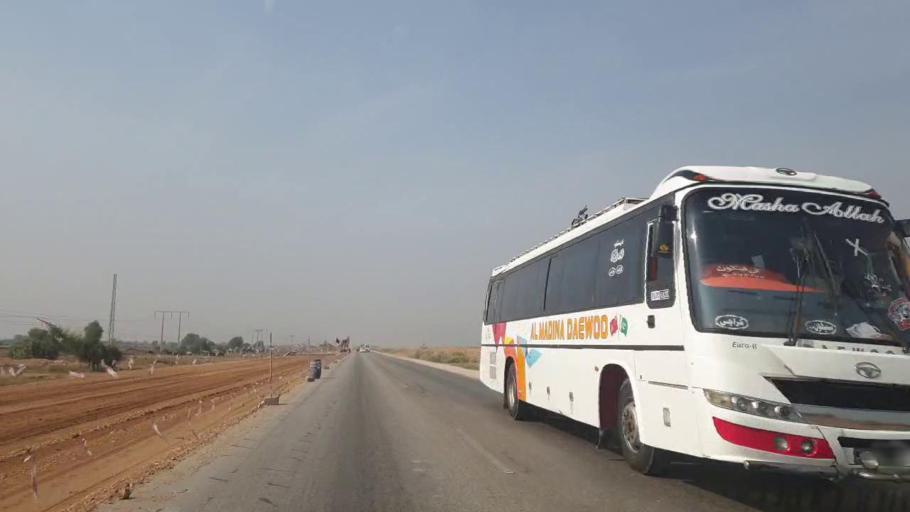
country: PK
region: Sindh
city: Sann
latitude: 26.1238
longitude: 68.0564
